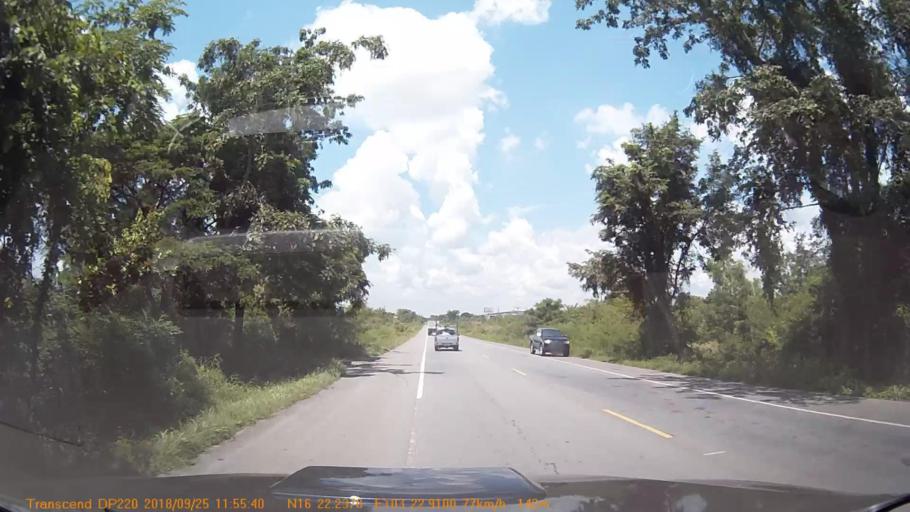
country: TH
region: Kalasin
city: Yang Talat
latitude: 16.3707
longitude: 103.3817
